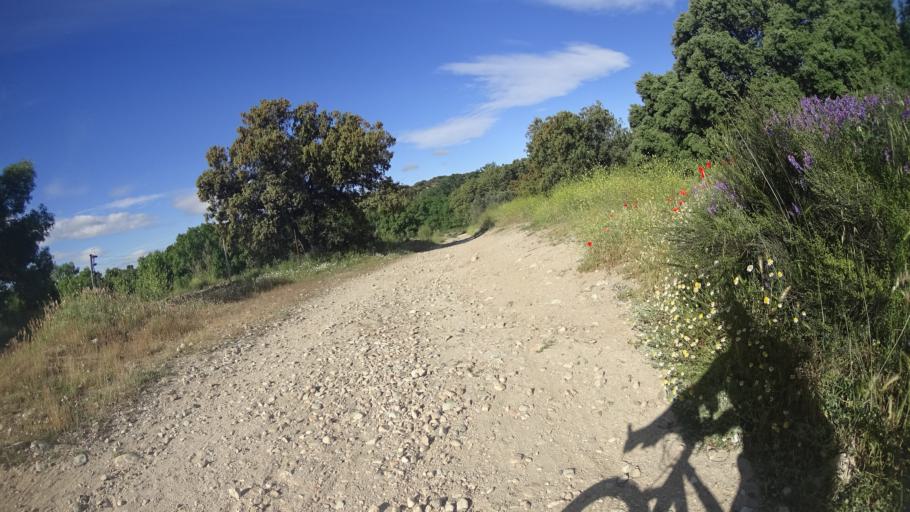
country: ES
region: Madrid
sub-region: Provincia de Madrid
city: Villanueva del Pardillo
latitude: 40.5102
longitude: -3.9382
